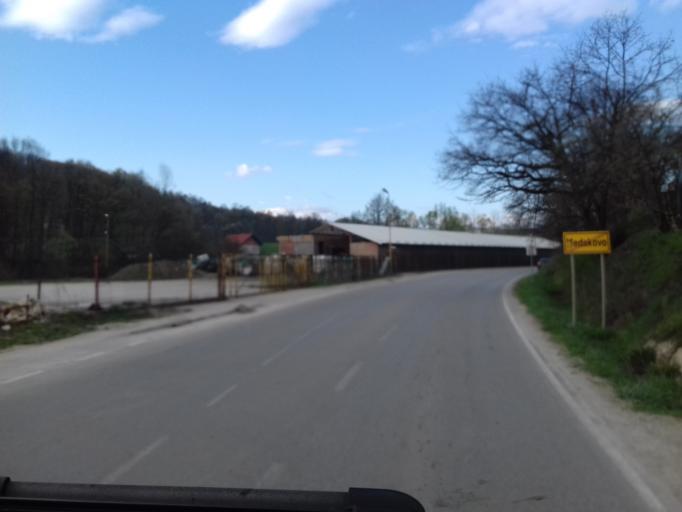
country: BA
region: Federation of Bosnia and Herzegovina
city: Tesanjka
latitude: 44.6368
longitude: 18.0123
